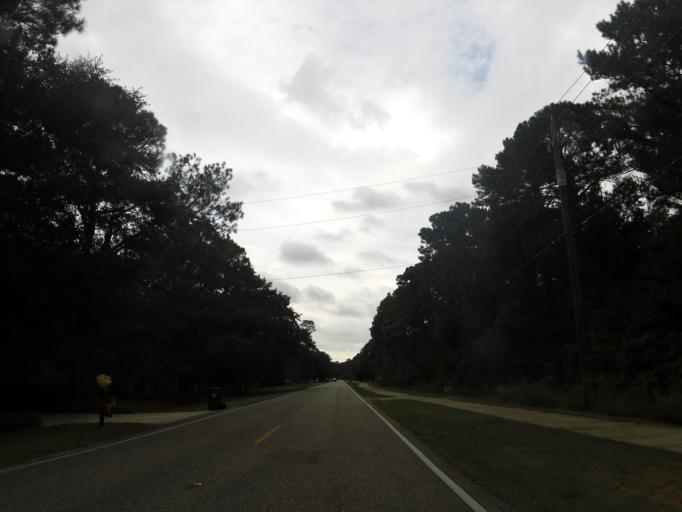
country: US
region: Alabama
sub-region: Baldwin County
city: Point Clear
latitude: 30.4405
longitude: -87.9119
